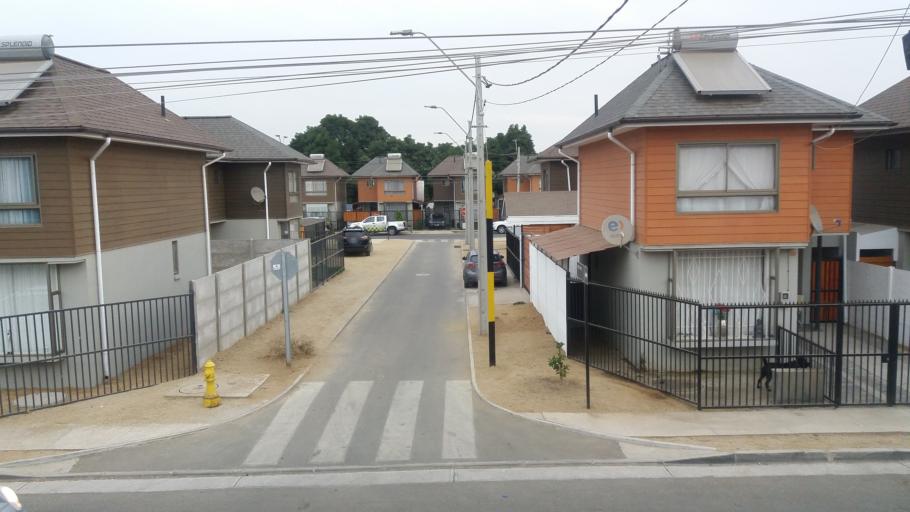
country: CL
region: Valparaiso
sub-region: Provincia de Quillota
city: Hacienda La Calera
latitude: -32.8330
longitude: -71.2263
